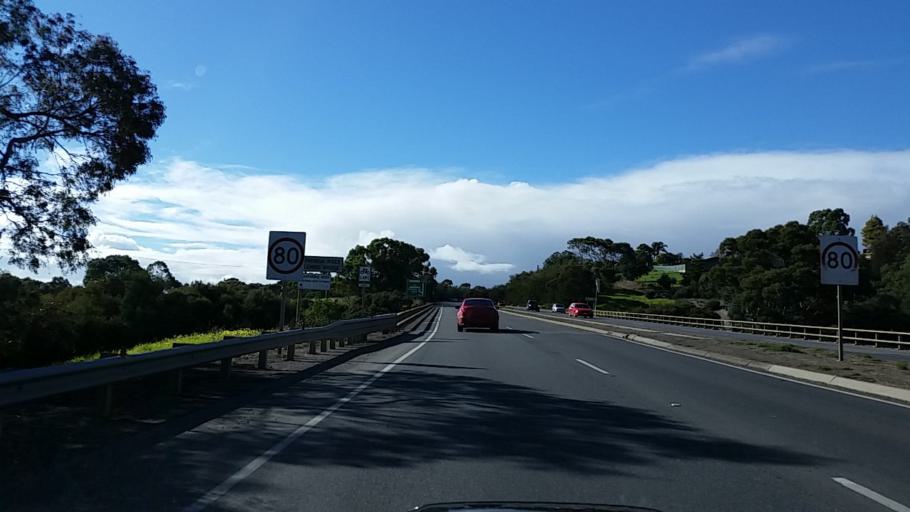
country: AU
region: South Australia
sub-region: Onkaparinga
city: Noarlunga
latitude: -35.1765
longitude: 138.4983
